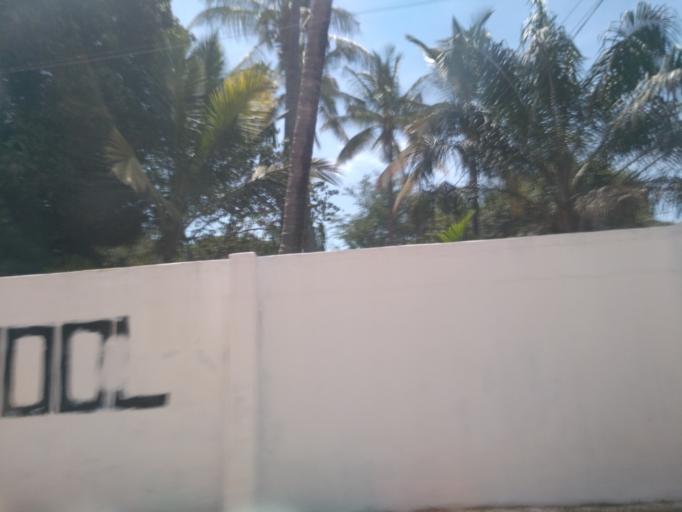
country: TZ
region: Mwanza
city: Mwanza
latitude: -2.5283
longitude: 32.8934
